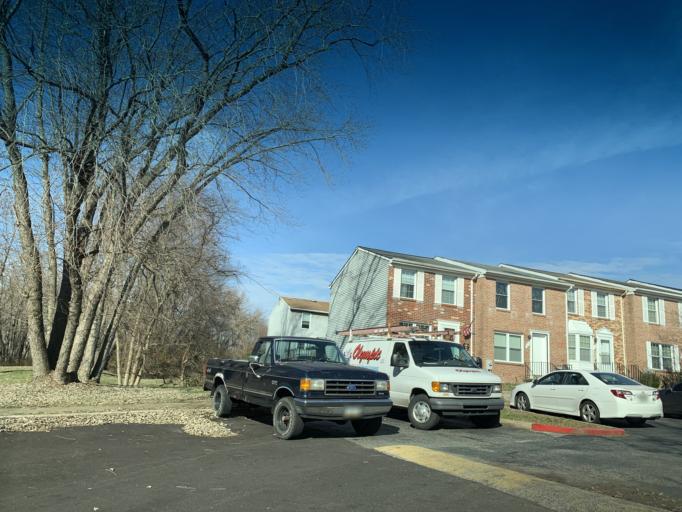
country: US
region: Maryland
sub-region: Harford County
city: South Bel Air
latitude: 39.5397
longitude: -76.3287
